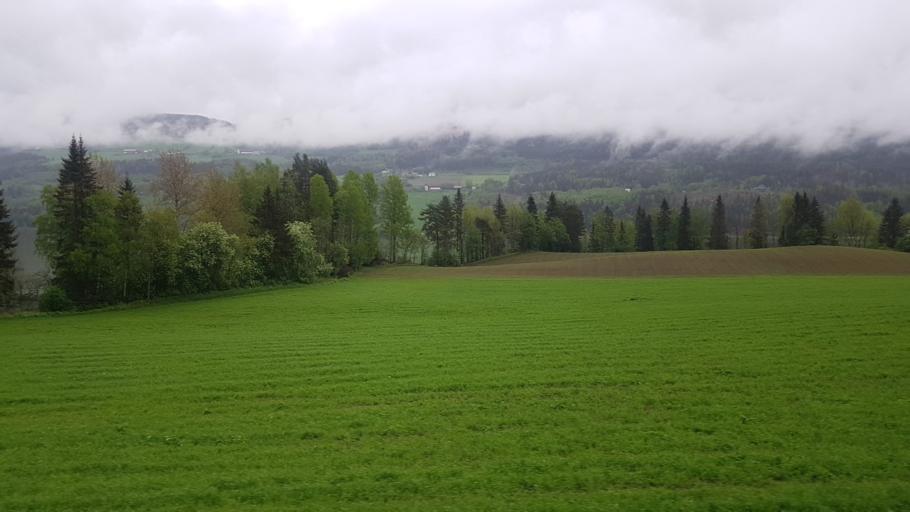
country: NO
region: Oppland
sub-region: Oyer
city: Tretten
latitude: 61.3358
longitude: 10.2850
